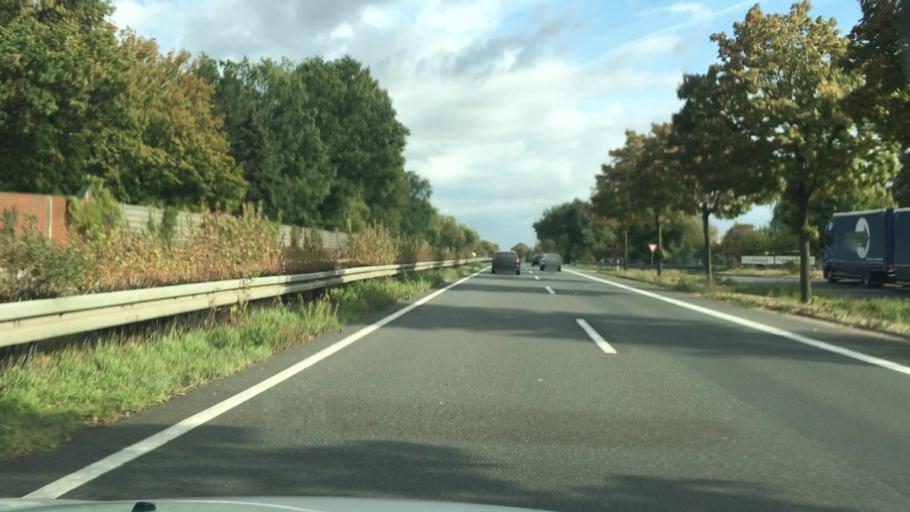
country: DE
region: Lower Saxony
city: Garbsen
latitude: 52.4556
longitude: 9.5479
